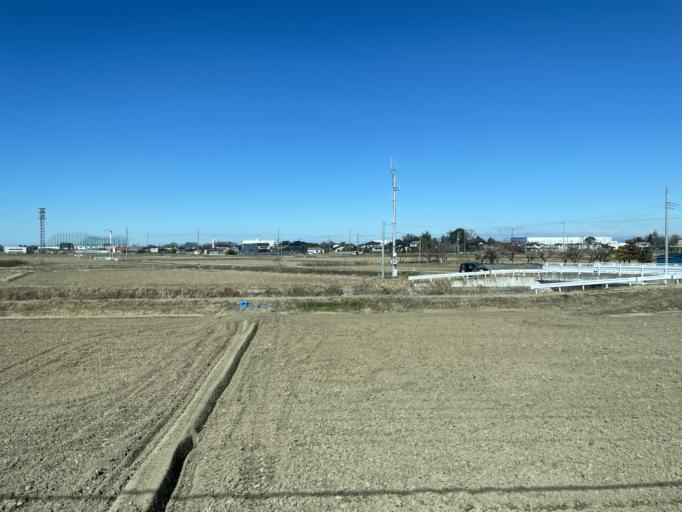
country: JP
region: Saitama
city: Kurihashi
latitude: 36.1152
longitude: 139.6826
